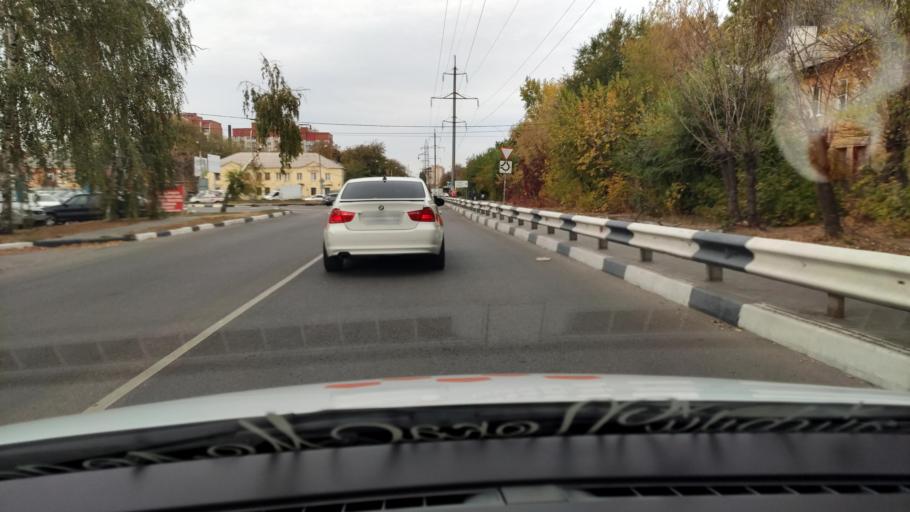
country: RU
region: Voronezj
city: Voronezh
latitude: 51.6910
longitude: 39.2153
